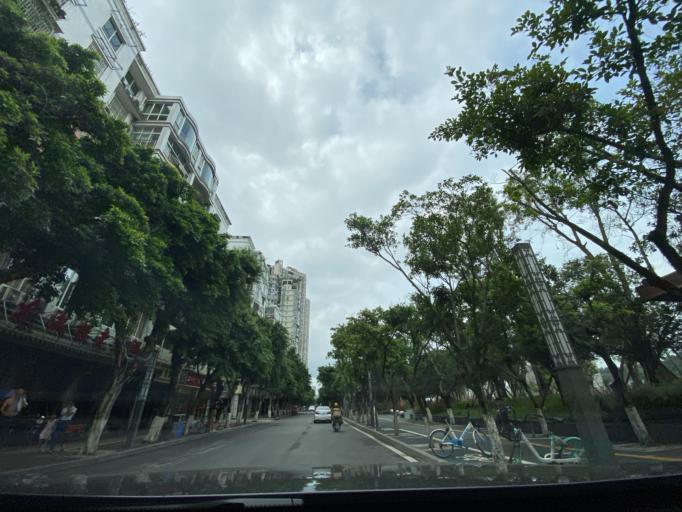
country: CN
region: Sichuan
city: Jiancheng
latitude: 30.3960
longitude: 104.5519
